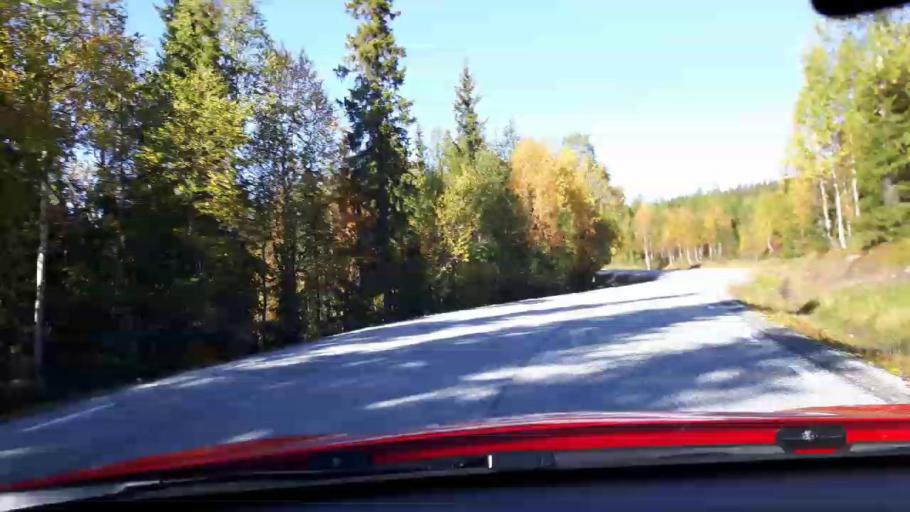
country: NO
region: Nord-Trondelag
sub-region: Royrvik
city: Royrvik
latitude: 64.8160
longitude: 14.1889
